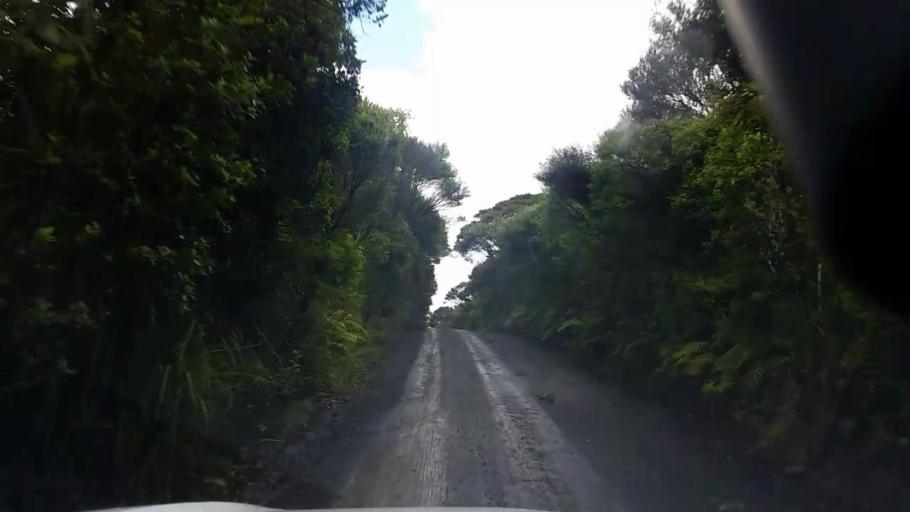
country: NZ
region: Auckland
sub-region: Auckland
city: Muriwai Beach
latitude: -36.9298
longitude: 174.5034
